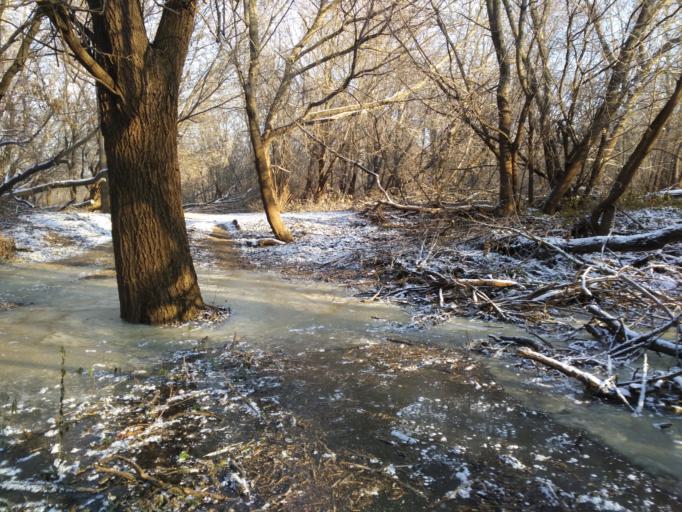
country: RU
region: Kirov
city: Vyatskiye Polyany
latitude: 56.2374
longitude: 51.0795
